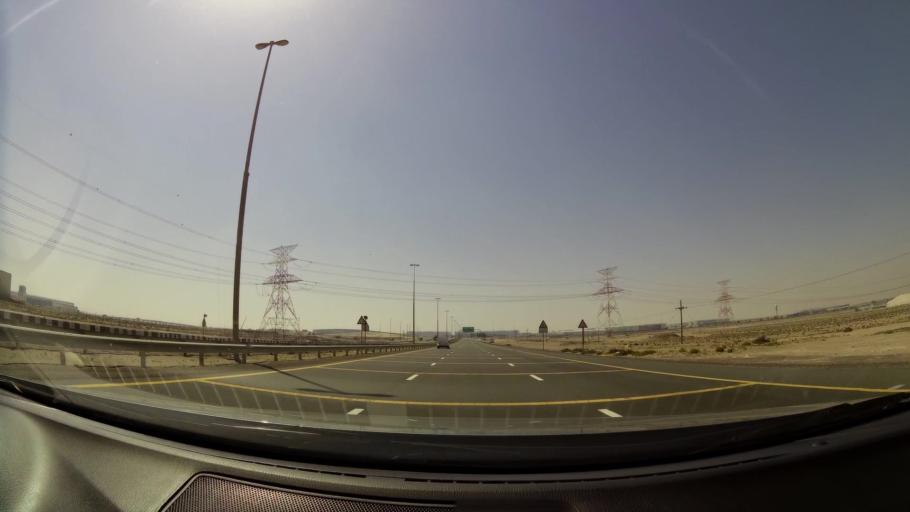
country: AE
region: Dubai
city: Dubai
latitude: 24.9239
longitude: 55.0969
